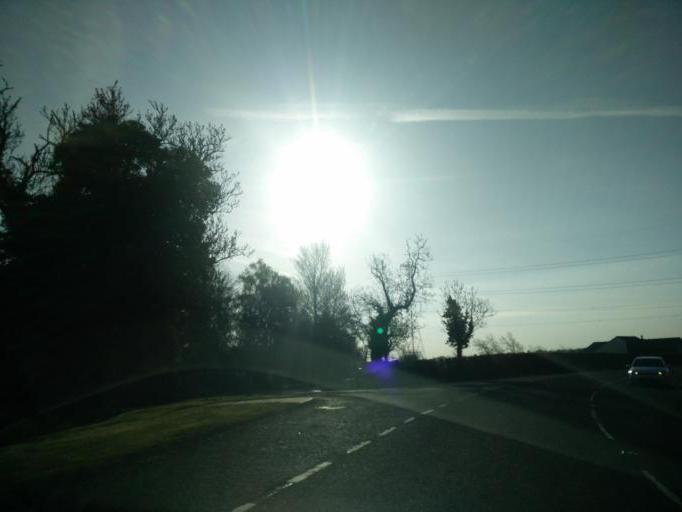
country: GB
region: England
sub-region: Stockton-on-Tees
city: Billingham
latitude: 54.6212
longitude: -1.3259
